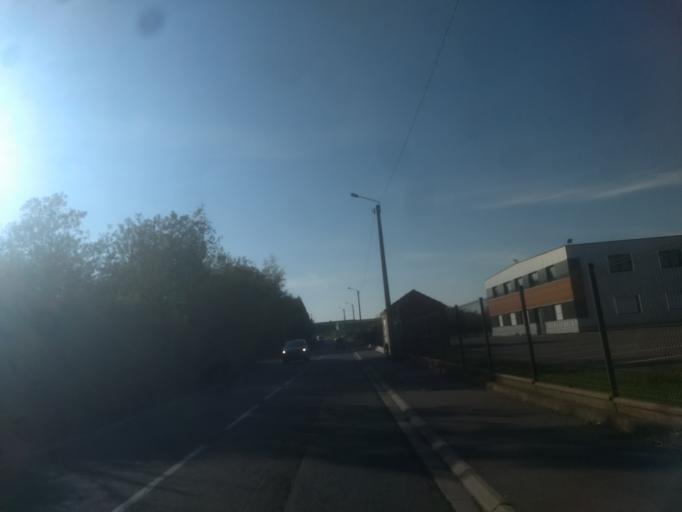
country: FR
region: Nord-Pas-de-Calais
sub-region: Departement du Pas-de-Calais
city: Achicourt
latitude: 50.2776
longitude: 2.7699
